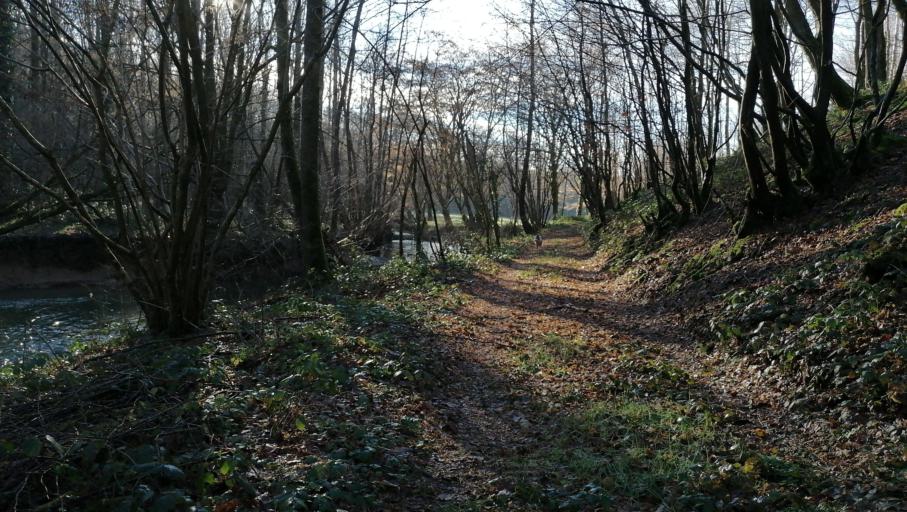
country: FR
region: Nord-Pas-de-Calais
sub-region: Departement du Nord
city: Recquignies
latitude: 50.2074
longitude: 4.0573
